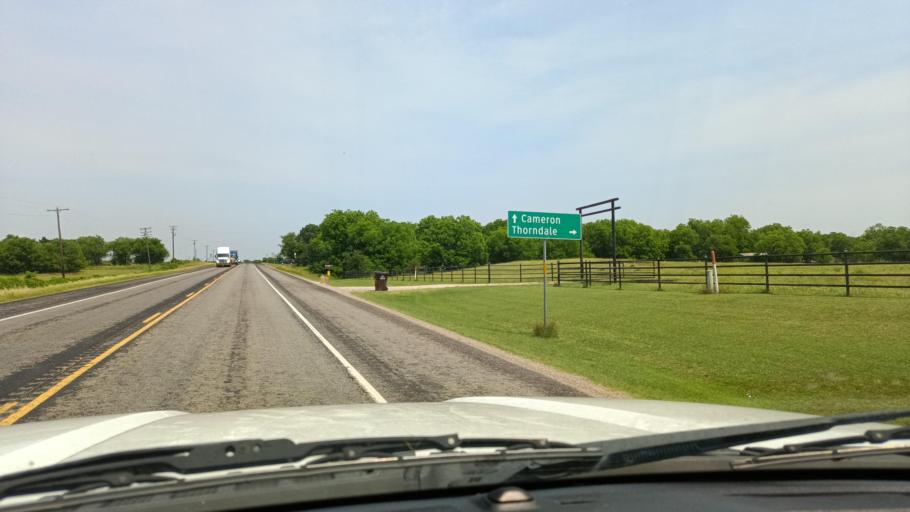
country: US
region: Texas
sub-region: Milam County
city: Cameron
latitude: 30.8507
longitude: -97.0834
